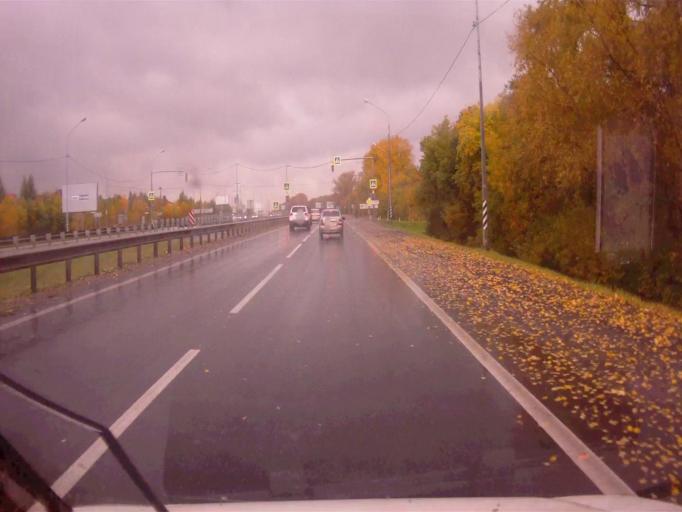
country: RU
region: Chelyabinsk
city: Dolgoderevenskoye
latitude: 55.2824
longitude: 61.3431
